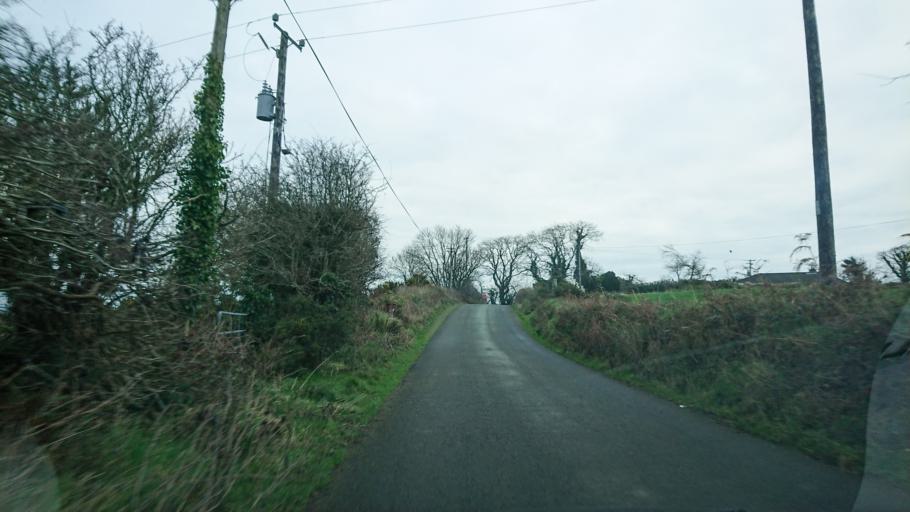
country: IE
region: Leinster
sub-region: Kilkenny
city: Mooncoin
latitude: 52.2104
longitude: -7.2642
